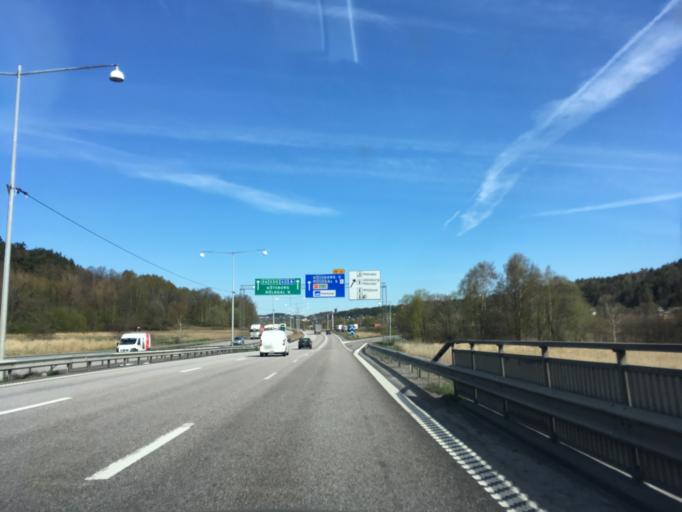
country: SE
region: Vaestra Goetaland
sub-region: Molndal
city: Kallered
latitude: 57.6280
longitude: 12.0357
